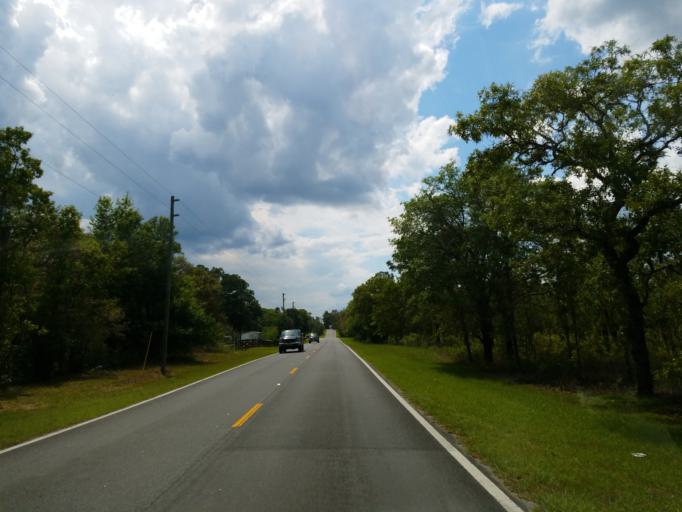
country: US
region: Florida
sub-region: Hernando County
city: Hill 'n Dale
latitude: 28.5357
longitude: -82.2710
